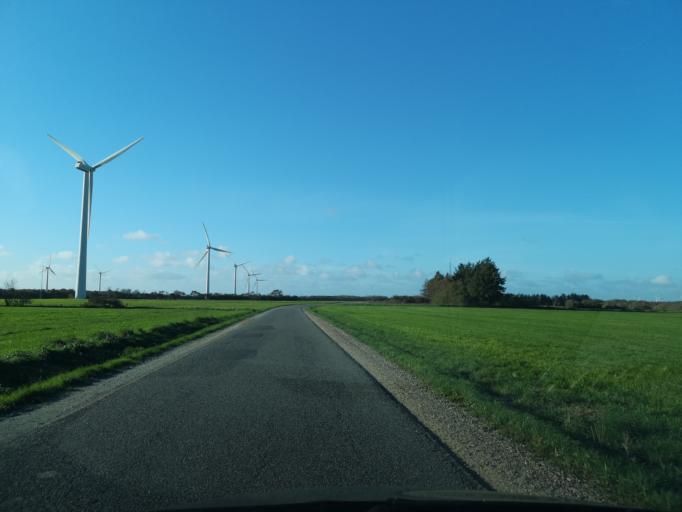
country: DK
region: Central Jutland
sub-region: Ringkobing-Skjern Kommune
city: Tarm
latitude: 55.8073
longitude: 8.4445
